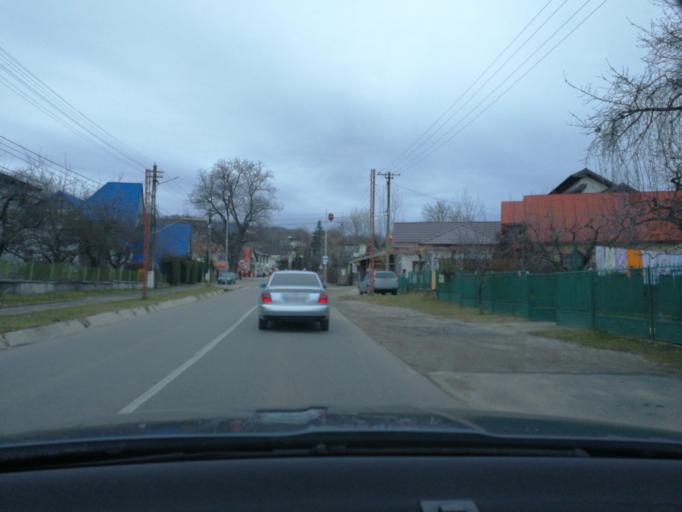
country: RO
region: Prahova
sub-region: Comuna Cornu
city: Cornu de Jos
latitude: 45.1488
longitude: 25.6912
